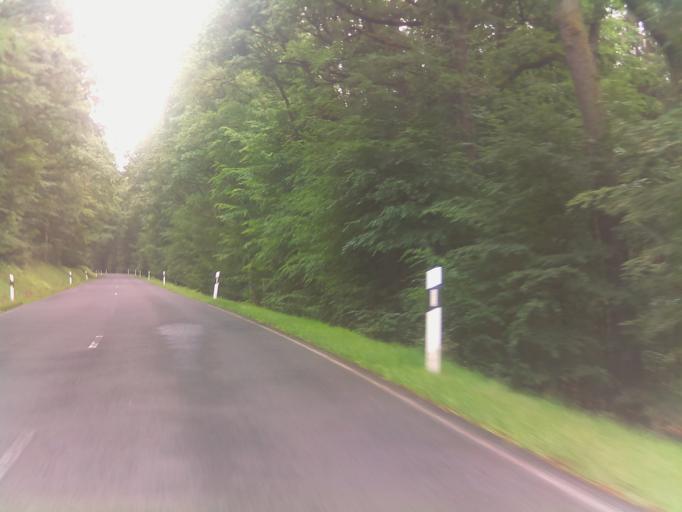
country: DE
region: Hesse
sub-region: Regierungsbezirk Darmstadt
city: Bad Orb
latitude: 50.2056
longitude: 9.4072
